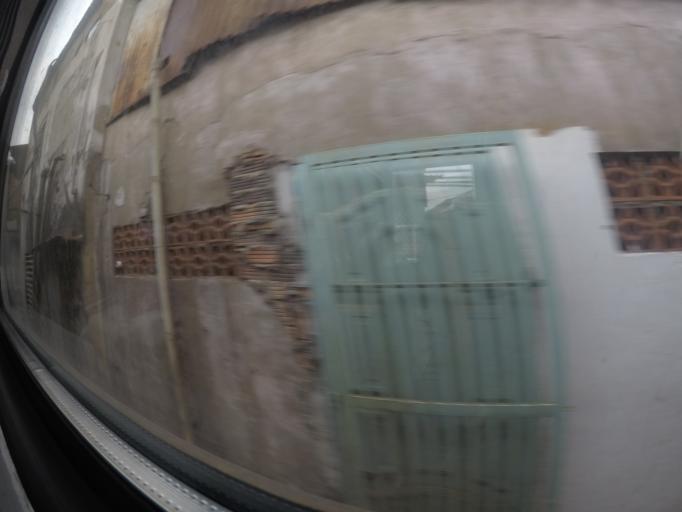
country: VN
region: Dong Nai
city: Bien Hoa
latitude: 10.9576
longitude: 106.8317
